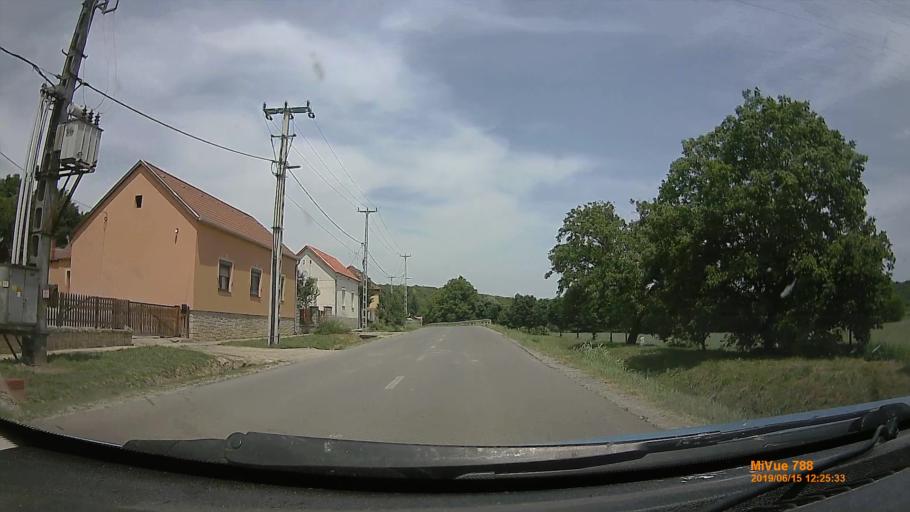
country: HU
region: Baranya
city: Buekkoesd
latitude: 46.1157
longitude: 17.9960
